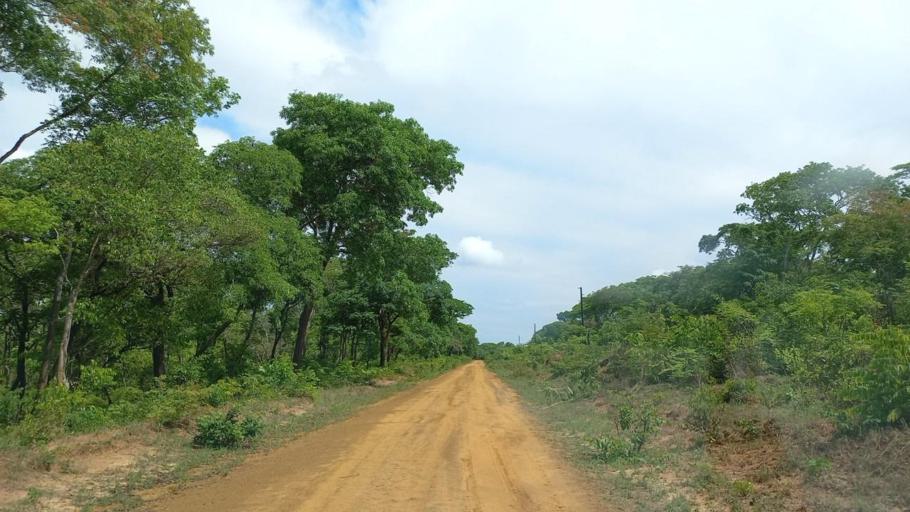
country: ZM
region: North-Western
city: Kabompo
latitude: -13.5359
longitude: 24.0966
